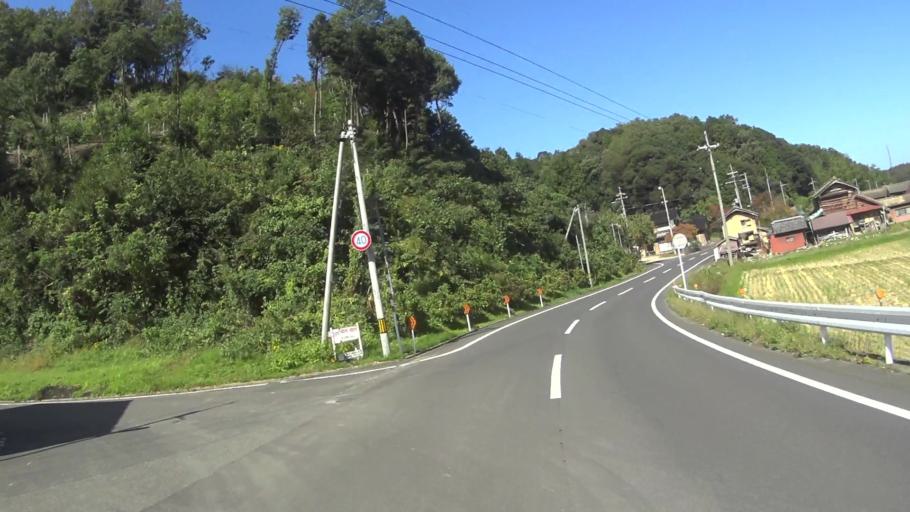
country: JP
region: Kyoto
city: Miyazu
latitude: 35.6602
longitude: 135.0601
